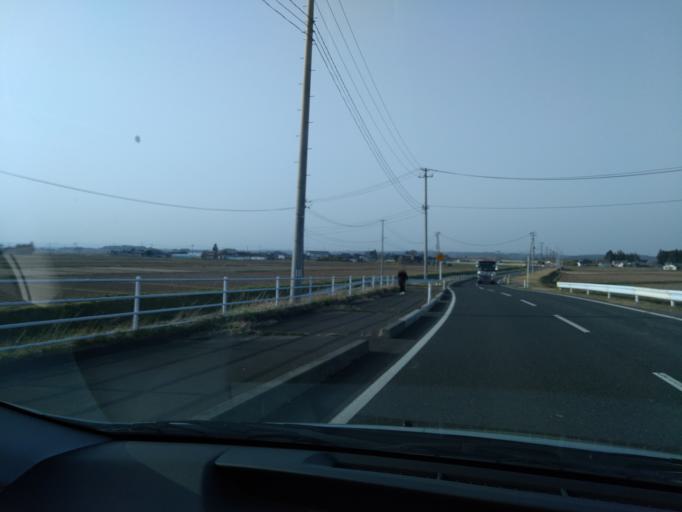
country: JP
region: Iwate
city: Ichinoseki
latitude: 38.7503
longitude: 141.1334
